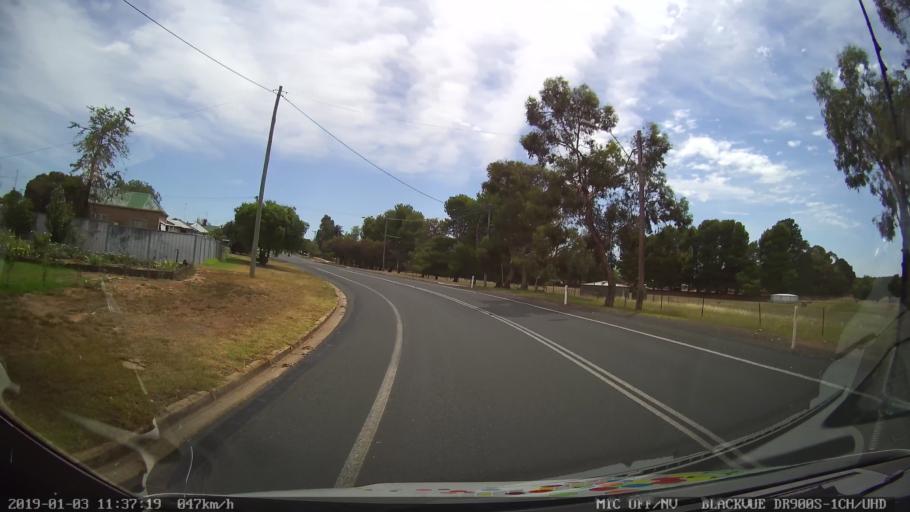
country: AU
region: New South Wales
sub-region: Weddin
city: Grenfell
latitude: -33.9038
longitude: 148.1609
